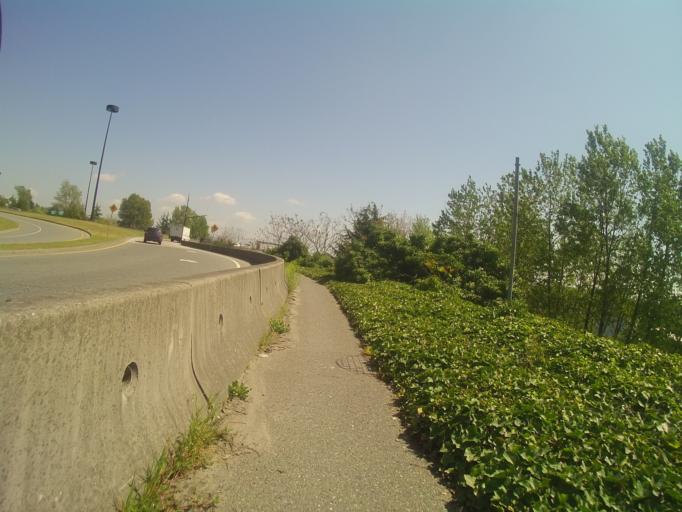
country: CA
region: British Columbia
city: Vancouver
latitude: 49.2101
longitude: -123.0786
